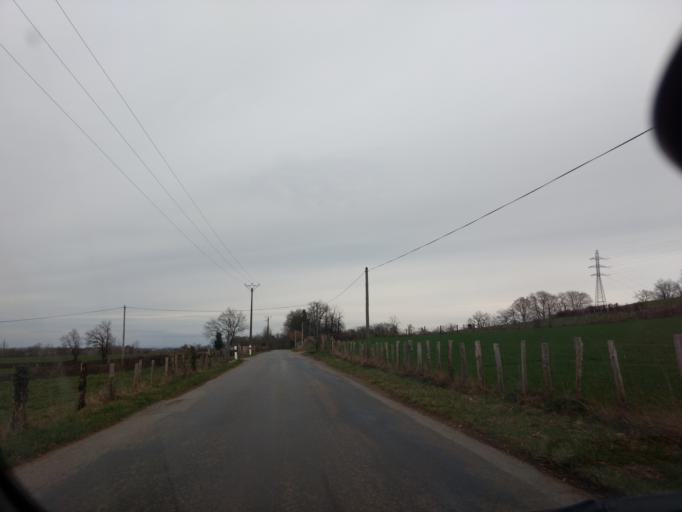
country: FR
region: Midi-Pyrenees
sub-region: Departement de l'Aveyron
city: Saint-Christophe-Vallon
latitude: 44.4313
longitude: 2.3505
